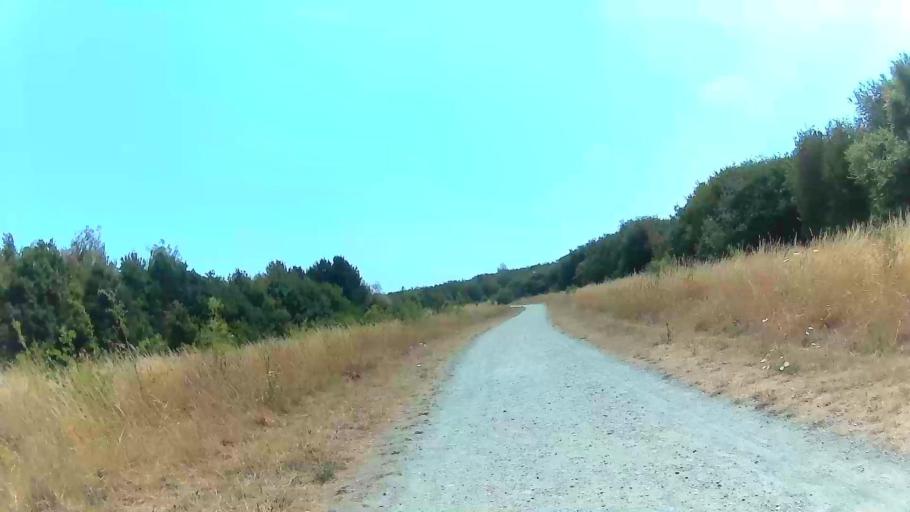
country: GB
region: England
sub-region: Greater London
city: Elm Park
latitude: 51.5290
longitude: 0.1934
